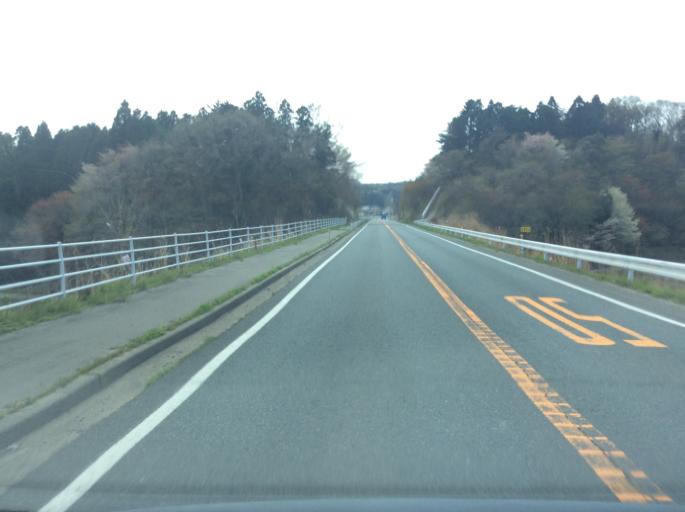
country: JP
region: Fukushima
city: Namie
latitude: 37.3289
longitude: 141.0164
